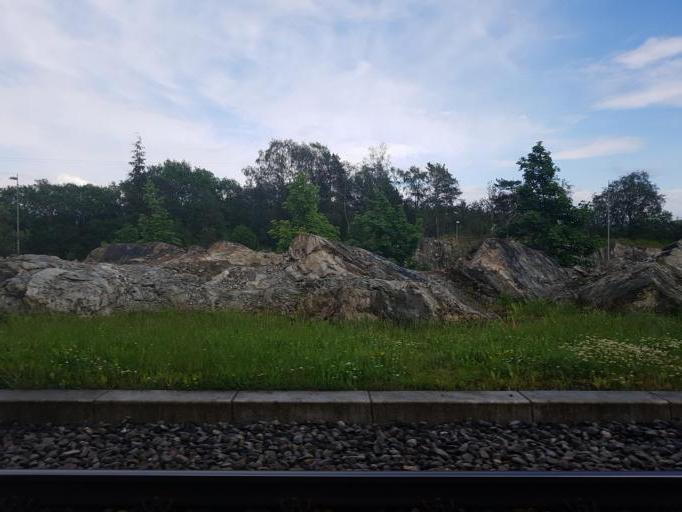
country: NO
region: Hordaland
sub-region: Bergen
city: Ytrebygda
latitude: 60.2942
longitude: 5.2684
